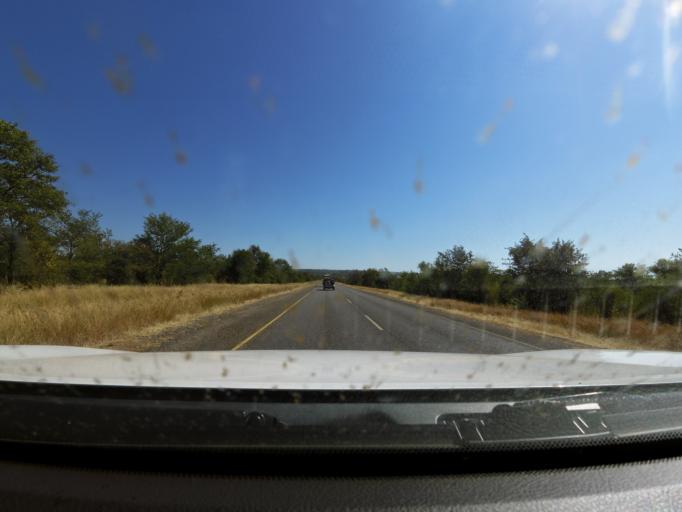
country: ZW
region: Matabeleland North
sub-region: Hwange District
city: Victoria Falls
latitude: -17.9712
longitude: 25.8257
